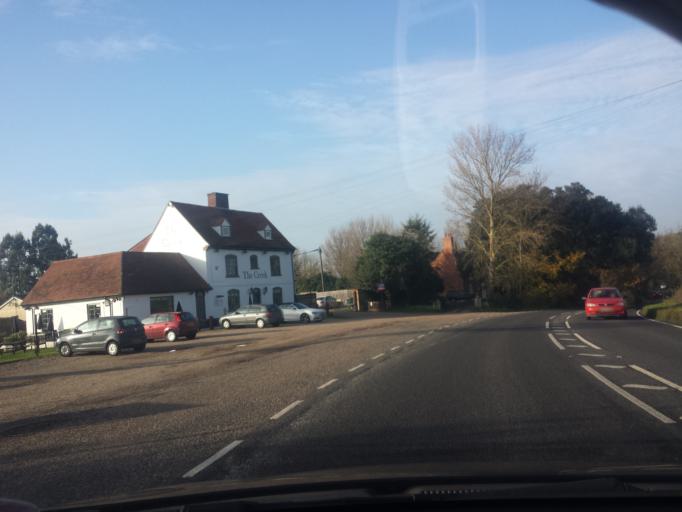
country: GB
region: England
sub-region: Essex
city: Saint Osyth
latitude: 51.8201
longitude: 1.0710
